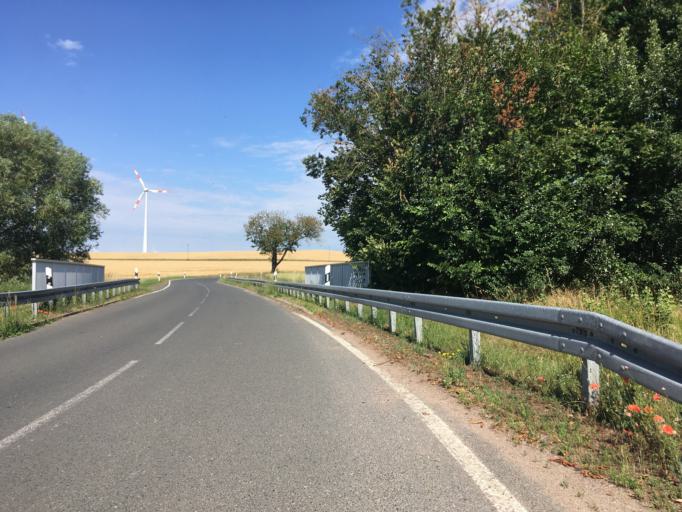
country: DE
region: Saxony-Anhalt
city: Baalberge
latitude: 51.7660
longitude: 11.8617
